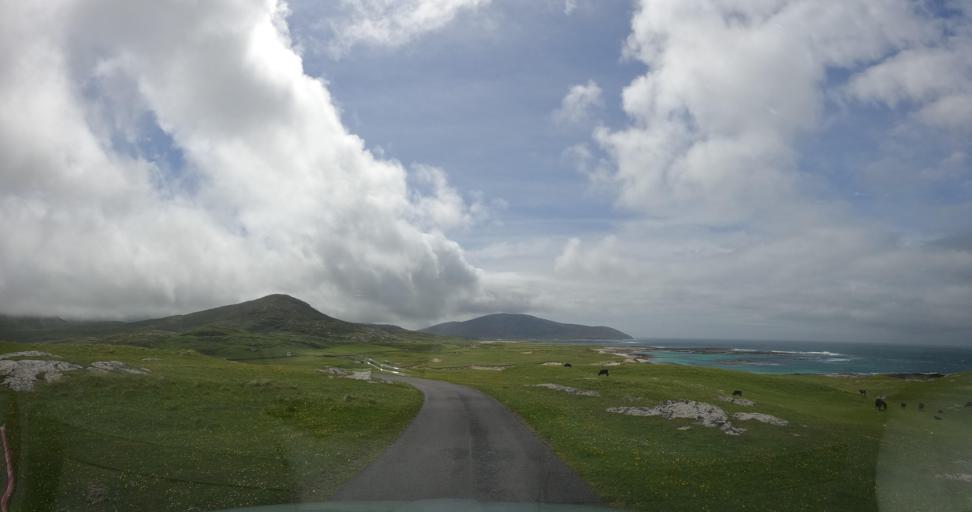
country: GB
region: Scotland
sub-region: Eilean Siar
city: Barra
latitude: 57.0076
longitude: -7.4997
